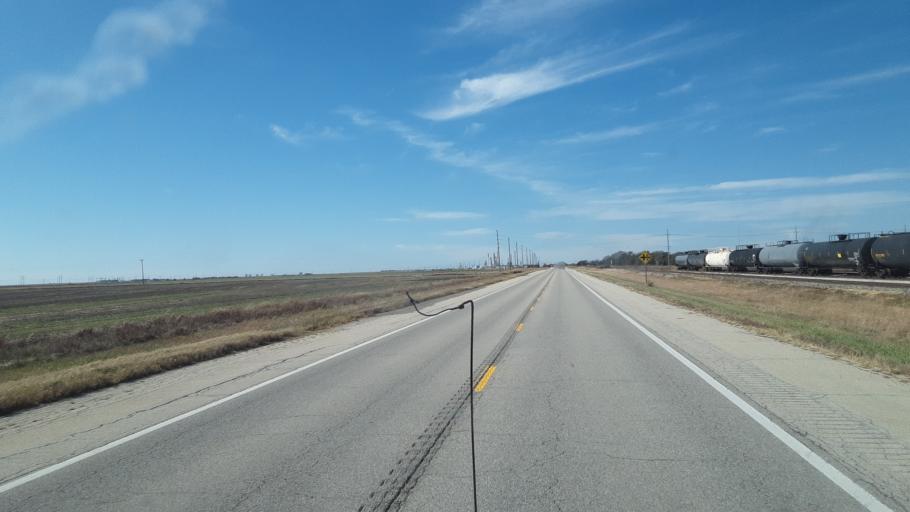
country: US
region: Kansas
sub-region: McPherson County
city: McPherson
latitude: 38.3752
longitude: -97.8111
